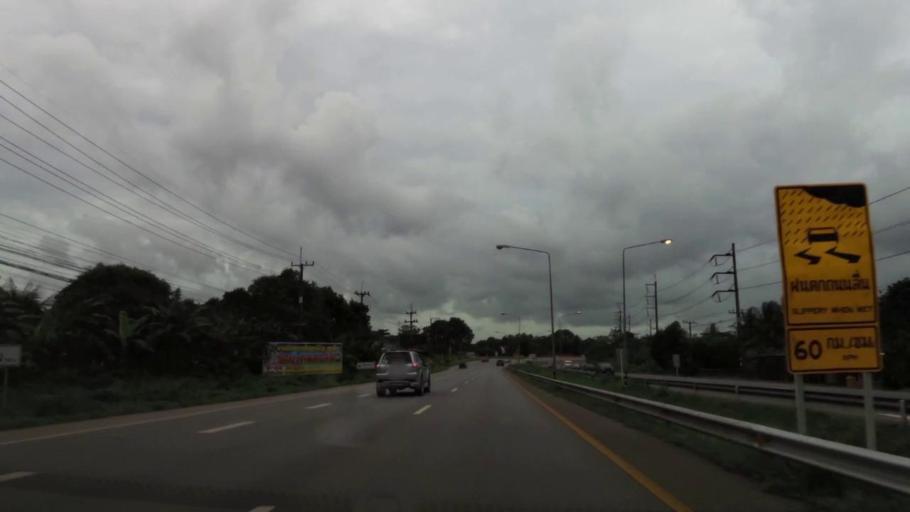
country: TH
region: Chanthaburi
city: Tha Mai
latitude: 12.6508
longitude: 102.0141
